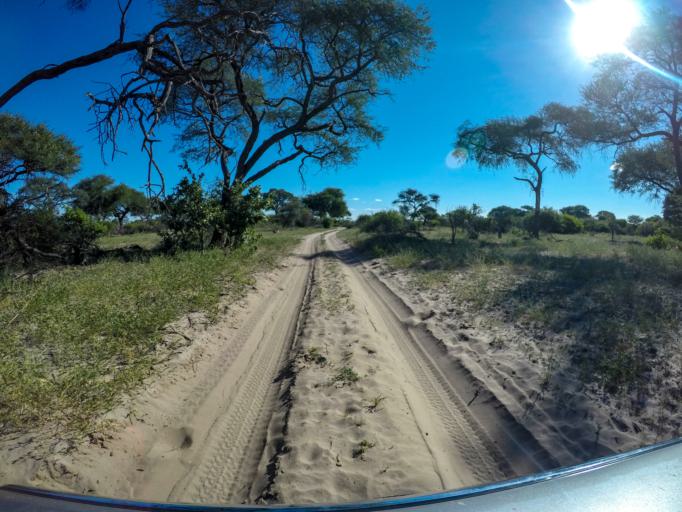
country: BW
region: Central
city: Rakops
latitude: -20.4551
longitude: 24.5180
